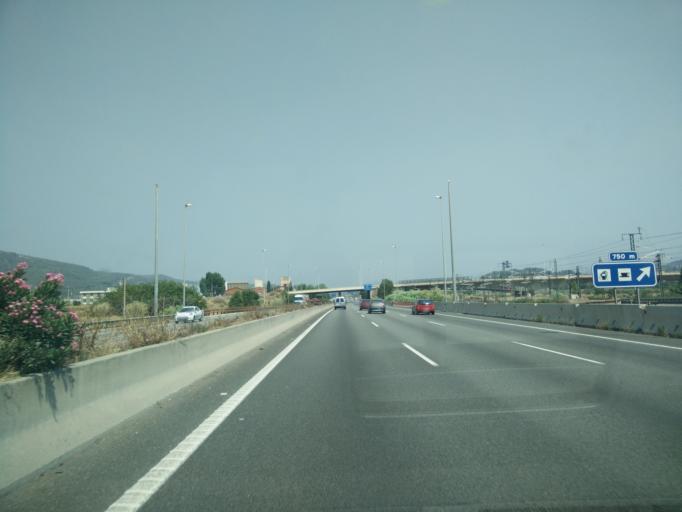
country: ES
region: Catalonia
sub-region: Provincia de Barcelona
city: Molins de Rei
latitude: 41.4053
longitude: 2.0113
